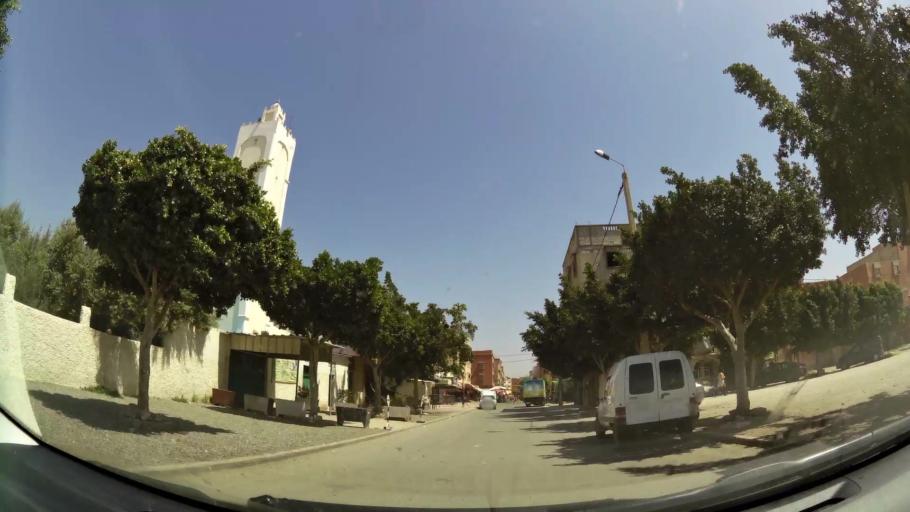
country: MA
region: Souss-Massa-Draa
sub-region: Inezgane-Ait Mellou
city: Inezgane
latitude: 30.3443
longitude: -9.4884
